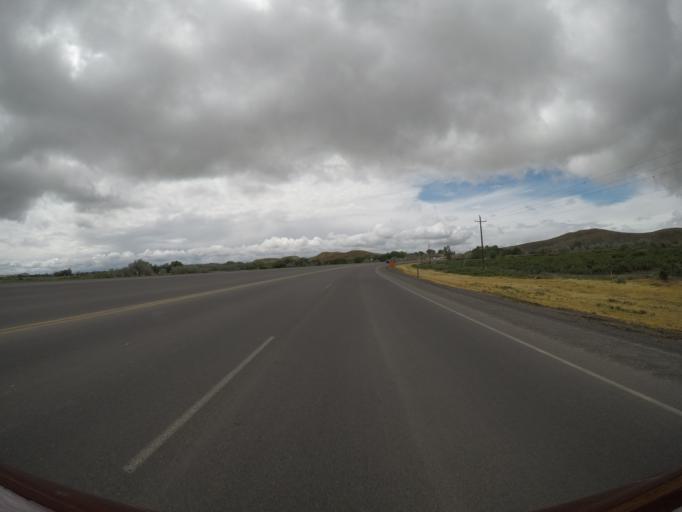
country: US
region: Wyoming
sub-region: Big Horn County
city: Lovell
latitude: 44.8371
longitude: -108.4276
